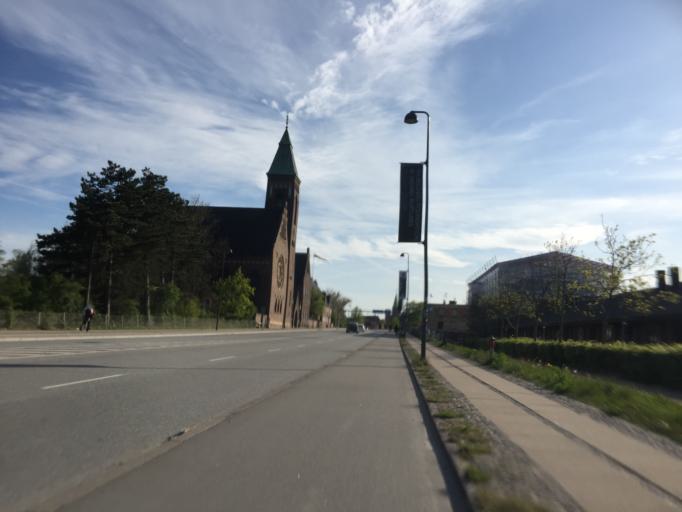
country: DK
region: Capital Region
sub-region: Kobenhavn
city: Christianshavn
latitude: 55.6933
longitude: 12.5910
